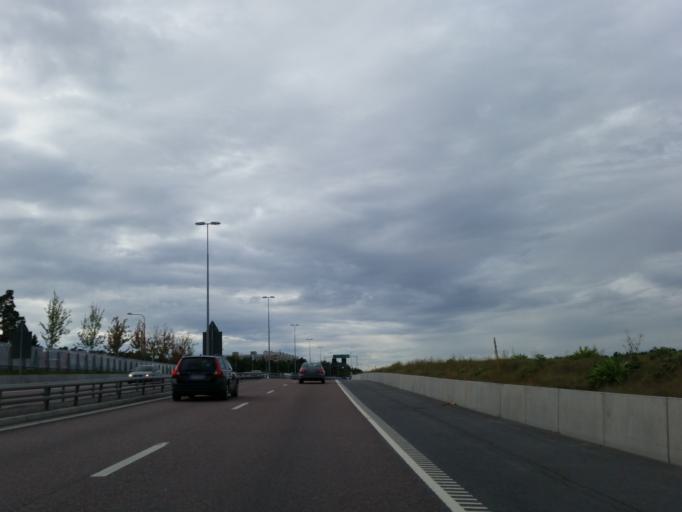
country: SE
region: Stockholm
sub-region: Stockholms Kommun
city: Kista
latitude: 59.3936
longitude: 17.9252
